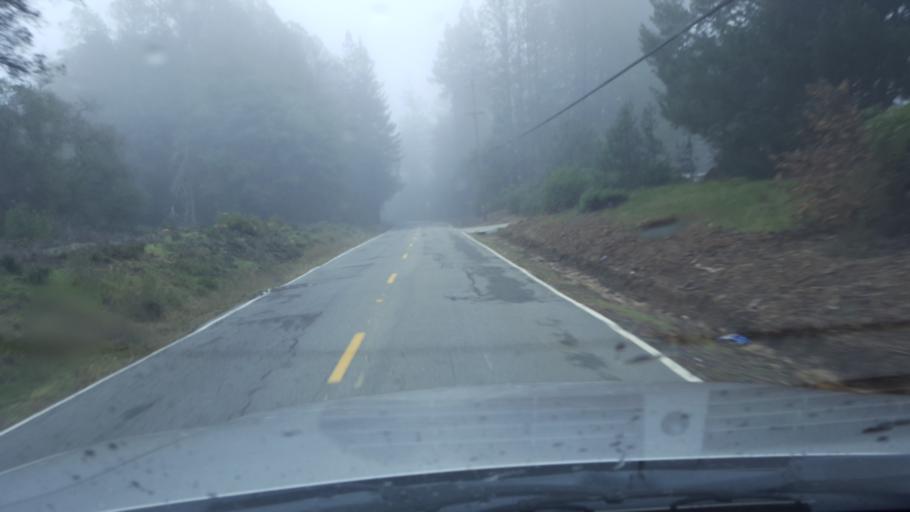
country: US
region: California
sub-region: Santa Cruz County
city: Corralitos
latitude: 37.0314
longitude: -121.7432
